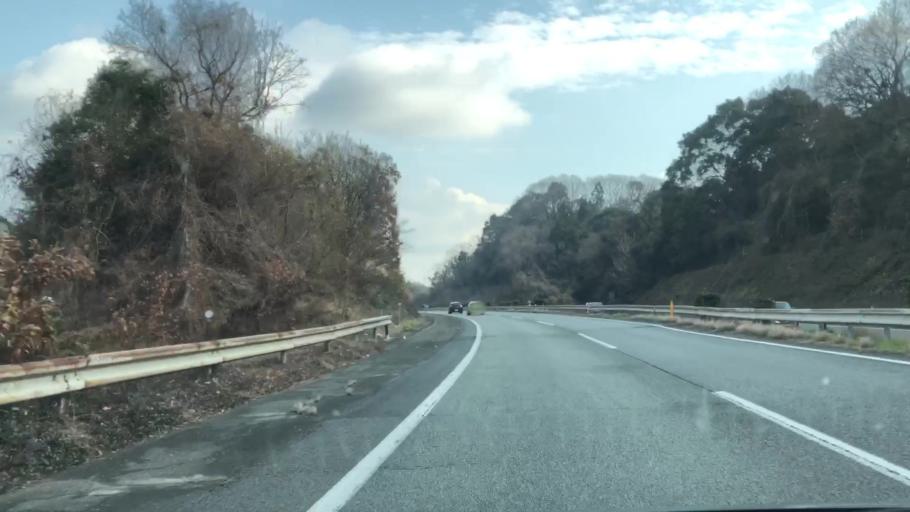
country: JP
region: Kumamoto
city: Tamana
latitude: 33.0034
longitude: 130.5847
